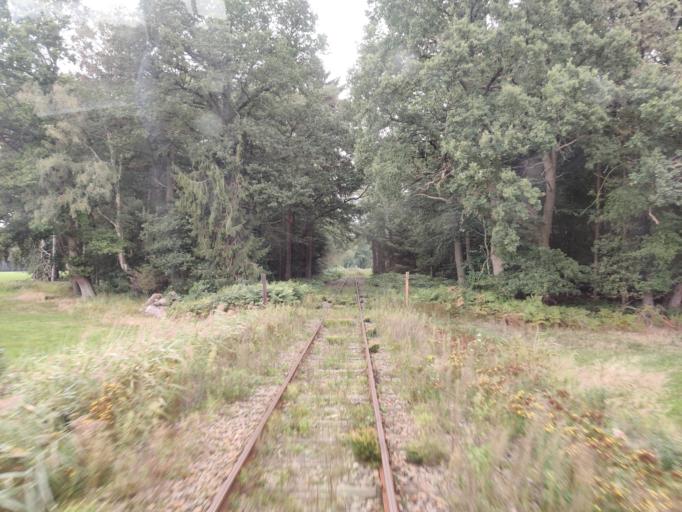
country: DE
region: Lower Saxony
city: Basdahl
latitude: 53.4307
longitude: 9.0146
